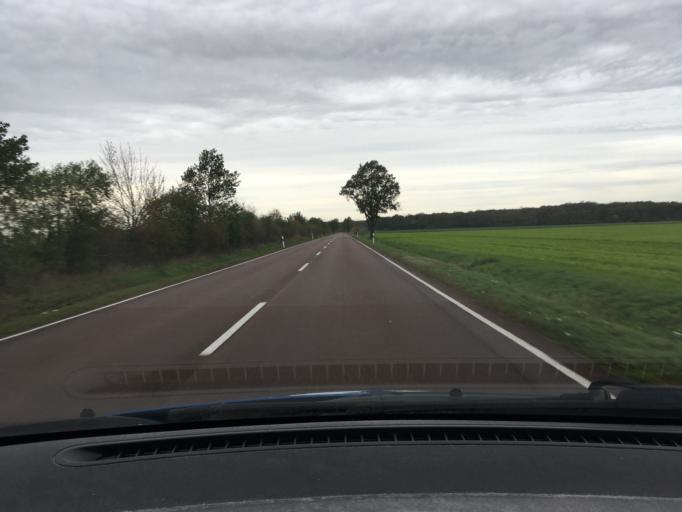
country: DE
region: Saxony-Anhalt
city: Leitzkau
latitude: 52.0266
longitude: 11.9995
